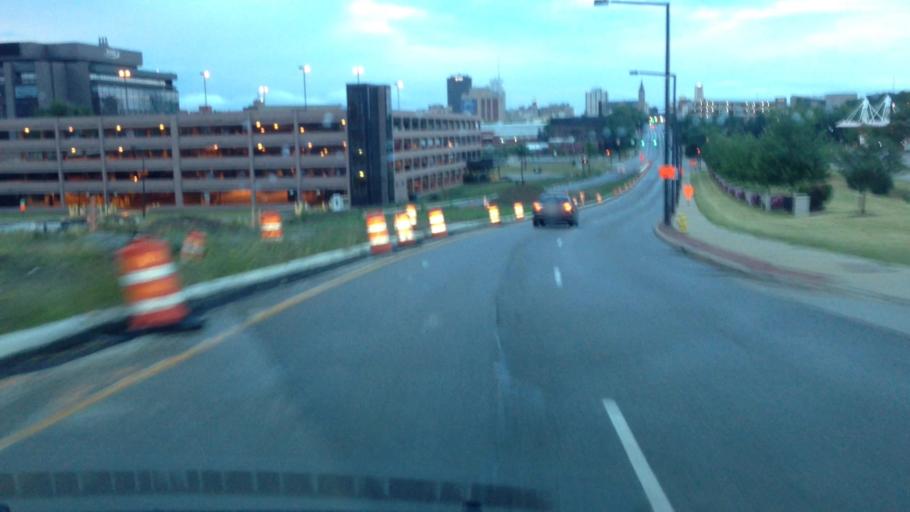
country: US
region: Ohio
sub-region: Summit County
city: Akron
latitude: 41.0688
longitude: -81.5244
